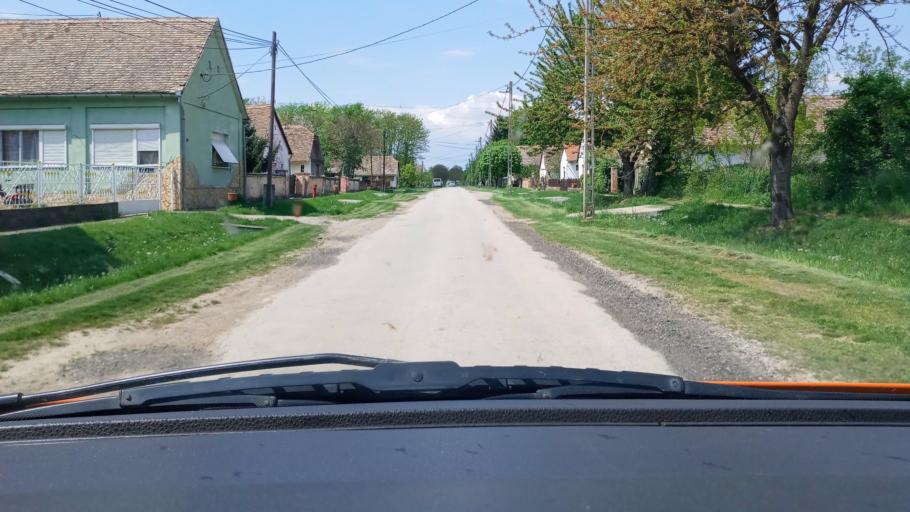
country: HR
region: Osjecko-Baranjska
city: Beli Manastir
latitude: 45.8031
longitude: 18.5209
